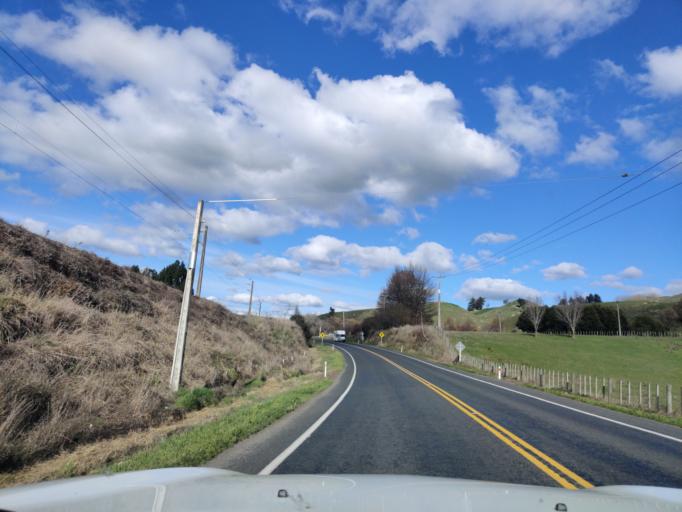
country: NZ
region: Manawatu-Wanganui
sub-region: Ruapehu District
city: Waiouru
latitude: -39.6887
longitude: 175.8081
